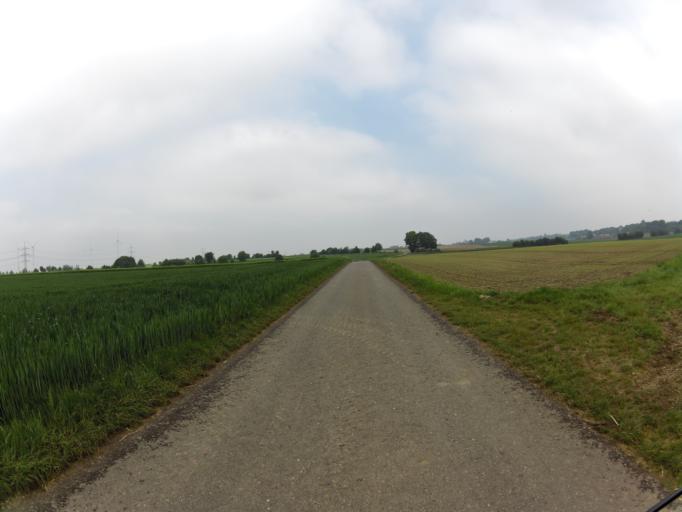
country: DE
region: North Rhine-Westphalia
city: Geilenkirchen
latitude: 51.0086
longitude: 6.1300
